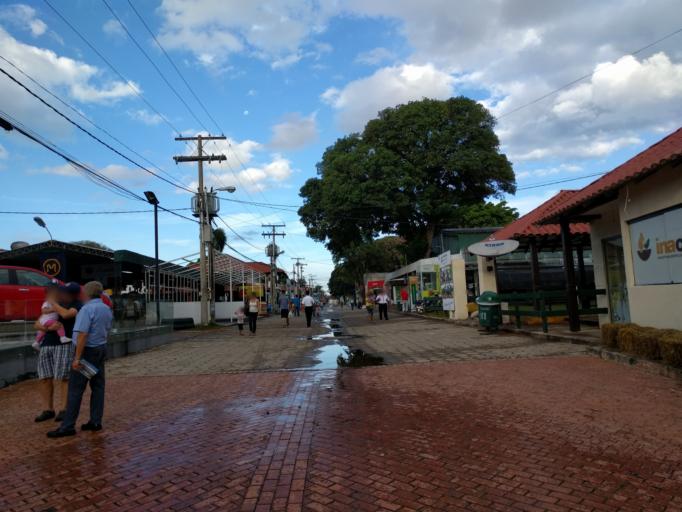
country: BO
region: Santa Cruz
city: Santa Cruz de la Sierra
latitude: -17.7840
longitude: -63.2110
